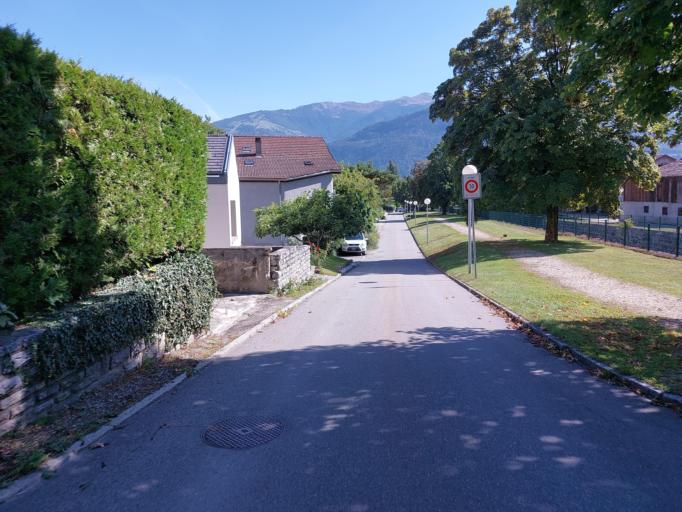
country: CH
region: Valais
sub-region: Conthey District
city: Ardon
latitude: 46.2166
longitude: 7.2574
